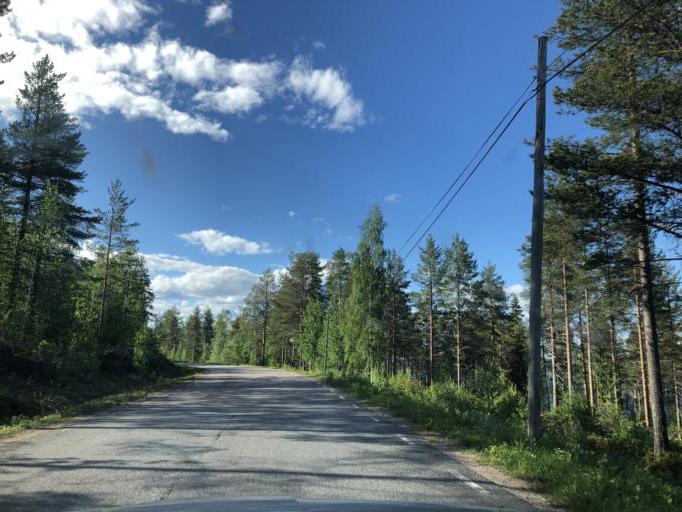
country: SE
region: Norrbotten
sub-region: Overkalix Kommun
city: OEverkalix
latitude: 66.3170
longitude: 22.8718
